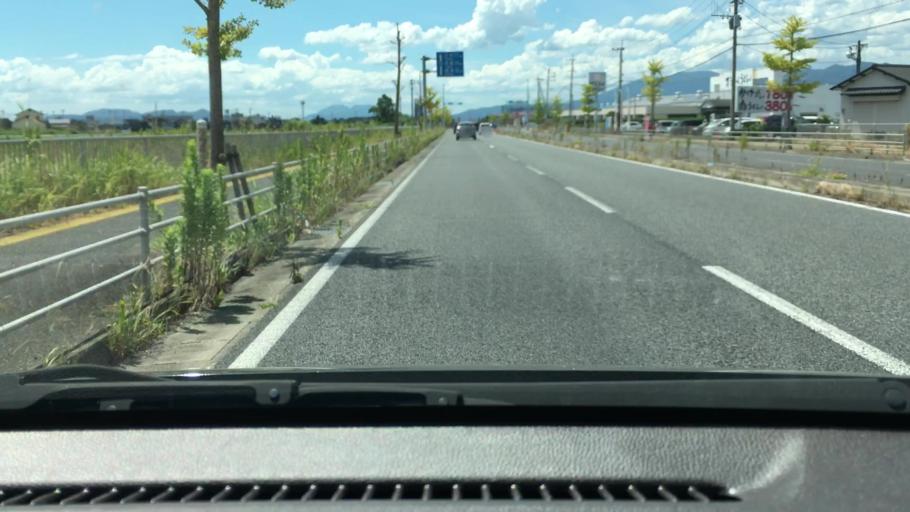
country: JP
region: Saga Prefecture
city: Saga-shi
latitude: 33.2740
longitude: 130.3318
